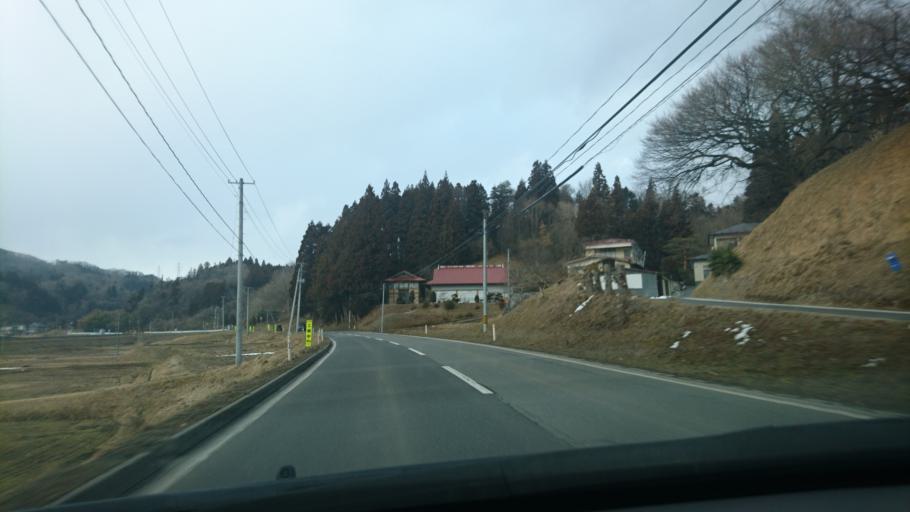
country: JP
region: Iwate
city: Ichinoseki
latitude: 38.9519
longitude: 141.3358
